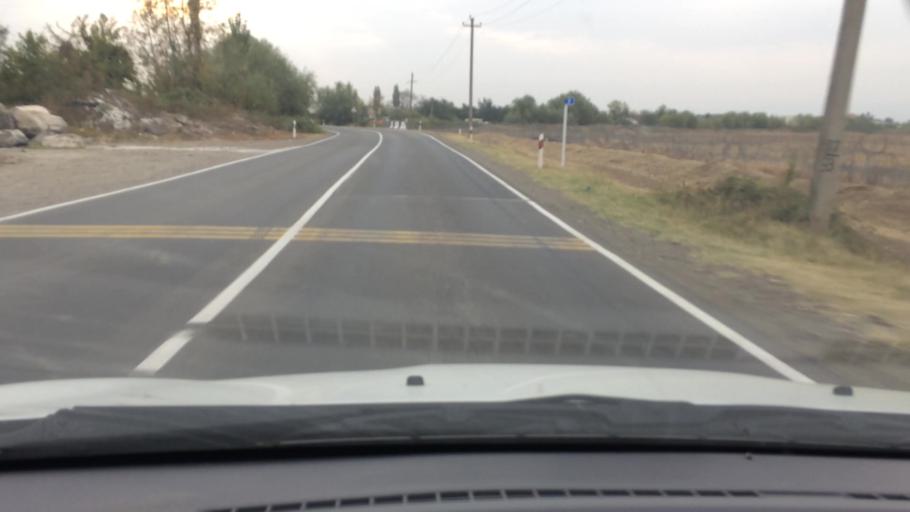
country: GE
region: Kvemo Kartli
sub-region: Marneuli
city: Marneuli
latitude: 41.4650
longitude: 44.8056
